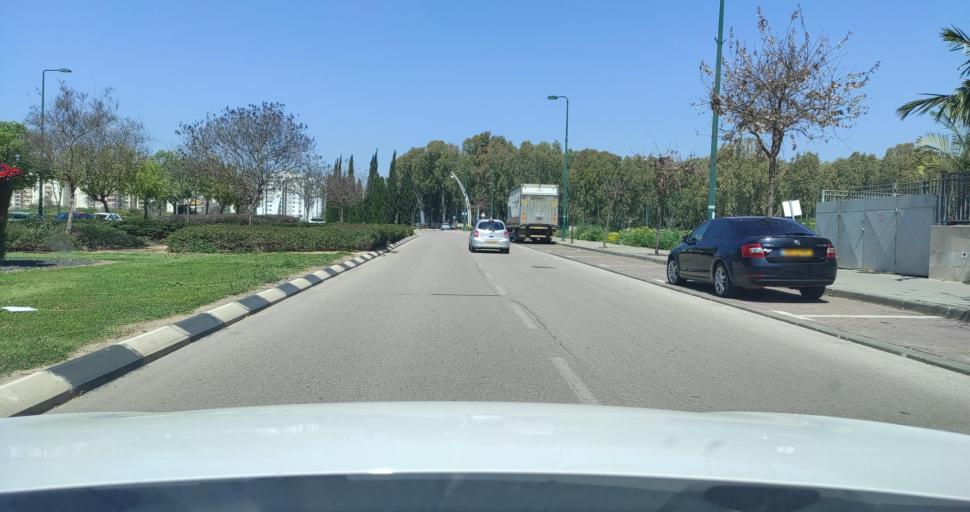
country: IL
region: Central District
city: Nordiyya
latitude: 32.3020
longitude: 34.8739
